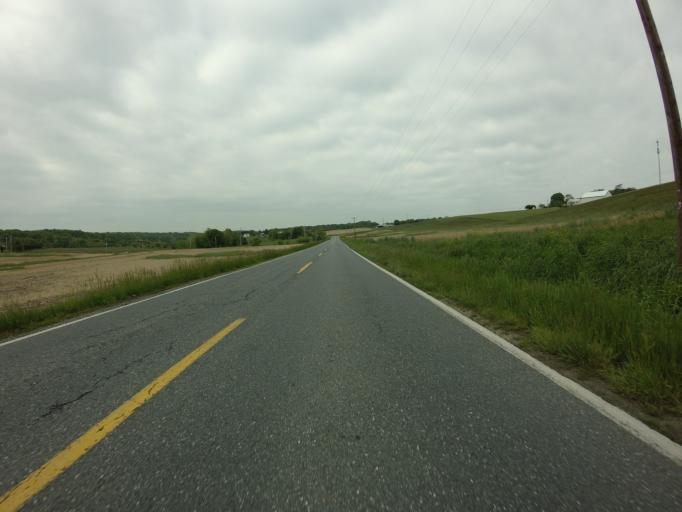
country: US
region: Maryland
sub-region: Frederick County
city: Green Valley
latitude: 39.2882
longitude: -77.2689
